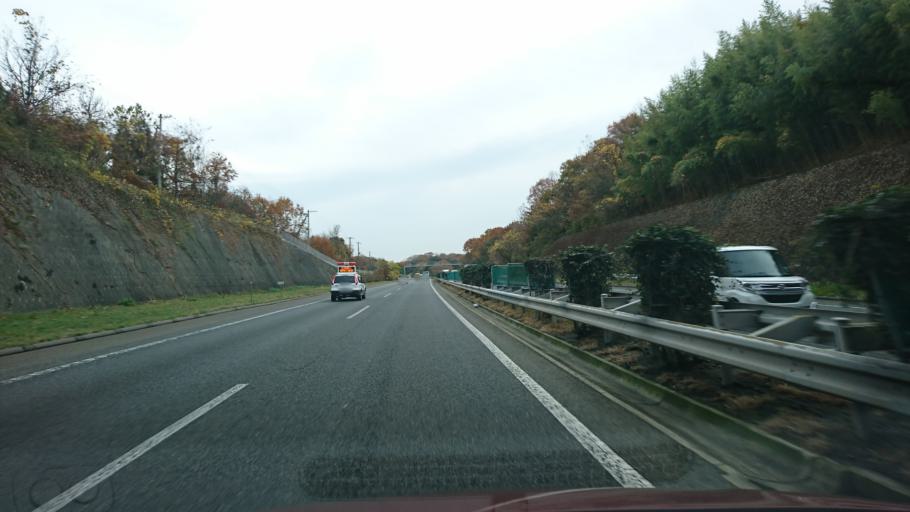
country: JP
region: Hyogo
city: Miki
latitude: 34.8213
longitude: 135.1095
